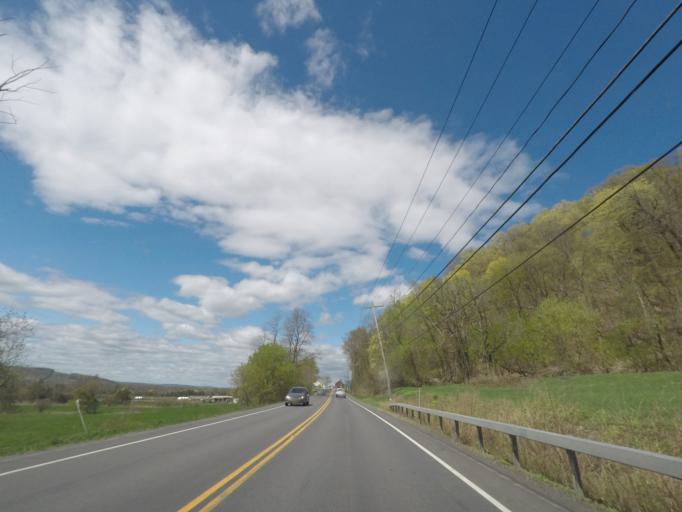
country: US
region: New York
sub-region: Columbia County
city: Oakdale
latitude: 42.2165
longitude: -73.7893
